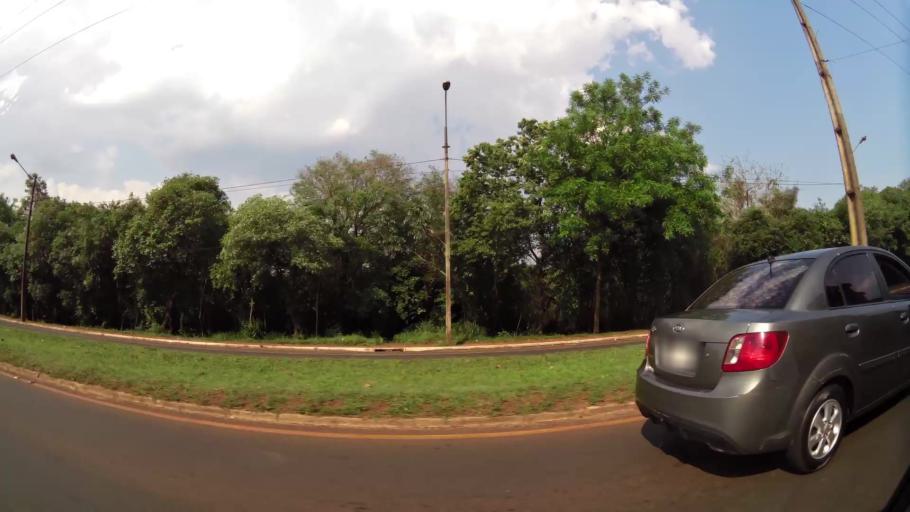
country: PY
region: Alto Parana
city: Presidente Franco
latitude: -25.5316
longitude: -54.6348
